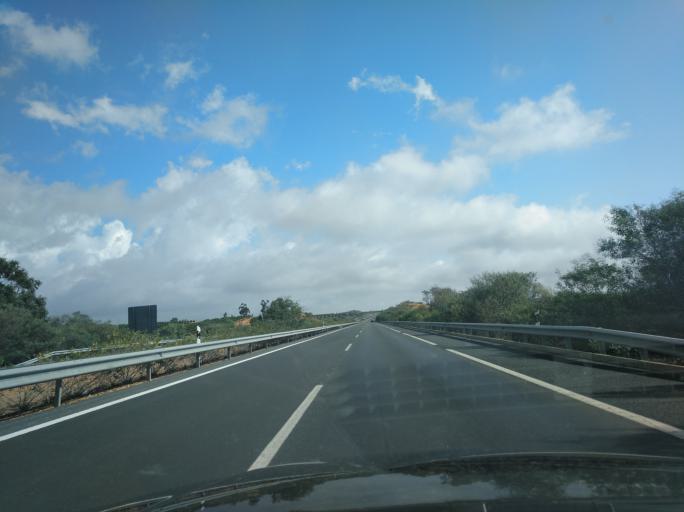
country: ES
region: Andalusia
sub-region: Provincia de Huelva
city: Villablanca
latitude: 37.2635
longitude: -7.2864
